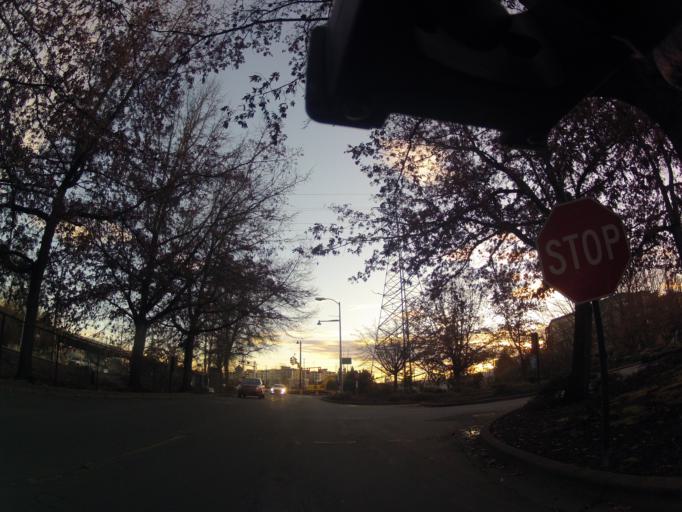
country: US
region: Washington
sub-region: King County
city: Renton
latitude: 47.5041
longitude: -122.2001
